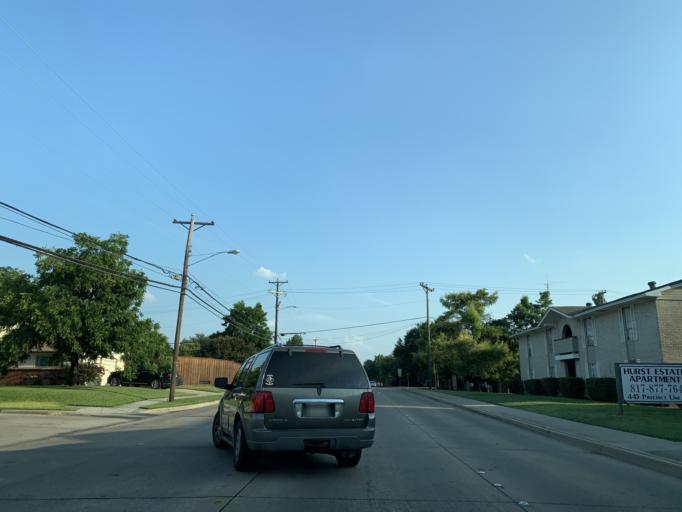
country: US
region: Texas
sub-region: Tarrant County
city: Hurst
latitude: 32.8170
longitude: -97.1865
